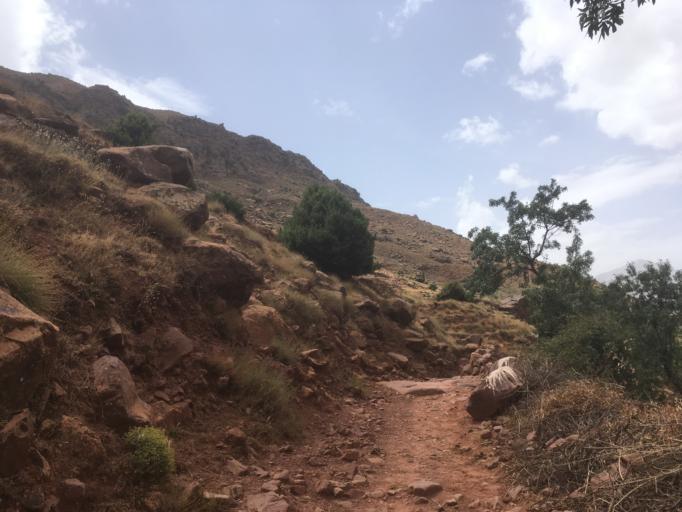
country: MA
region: Marrakech-Tensift-Al Haouz
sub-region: Al-Haouz
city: Tidili Mesfioua
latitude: 31.2952
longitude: -7.6690
